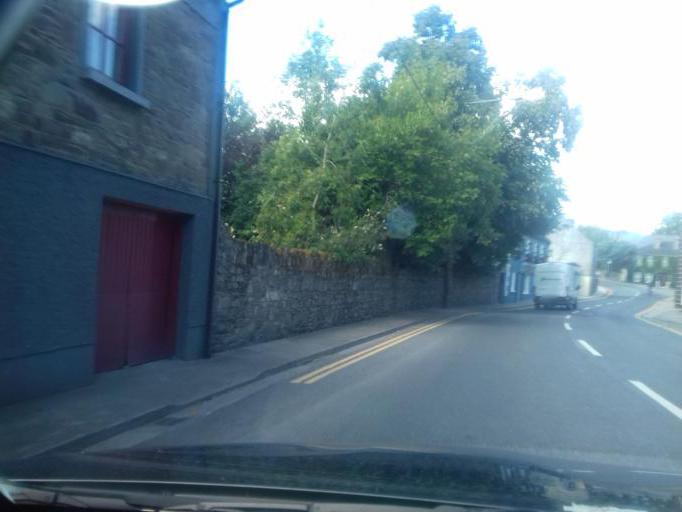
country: IE
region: Leinster
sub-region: Kilkenny
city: Thomastown
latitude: 52.5234
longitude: -7.1377
